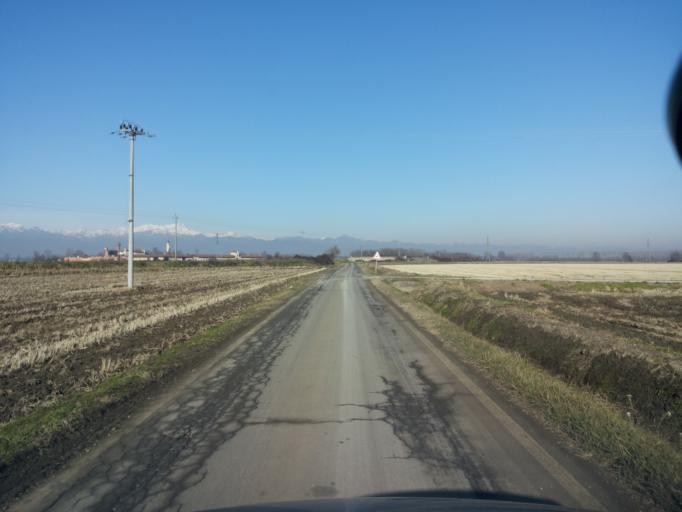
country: IT
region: Piedmont
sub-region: Provincia di Vercelli
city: San Germano Vercellese
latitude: 45.3866
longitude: 8.2443
